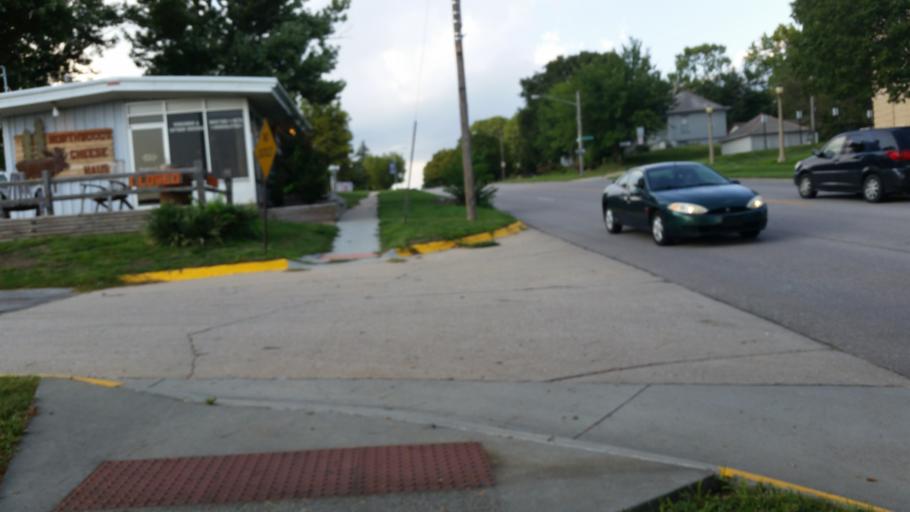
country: US
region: Nebraska
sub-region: Sarpy County
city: Papillion
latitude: 41.1584
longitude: -96.0431
